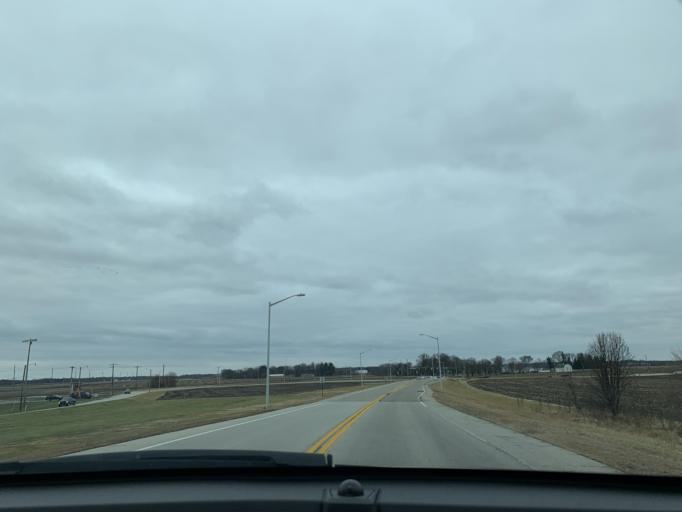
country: US
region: Illinois
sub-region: Sangamon County
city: Jerome
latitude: 39.7407
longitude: -89.6879
